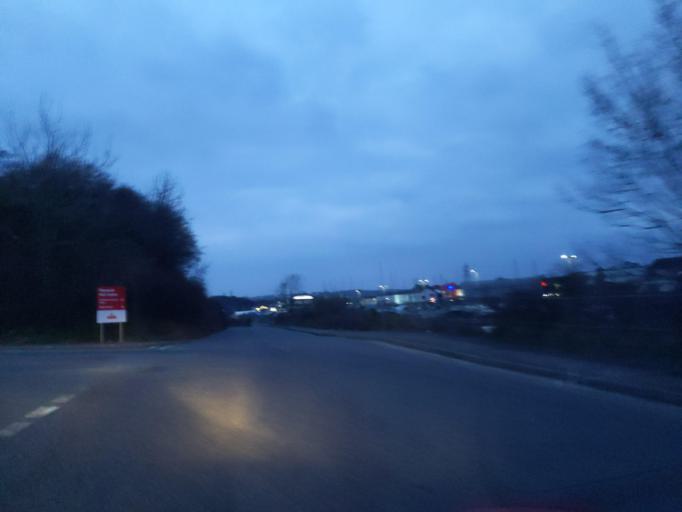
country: GB
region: England
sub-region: Plymouth
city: Plymstock
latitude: 50.3656
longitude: -4.1022
